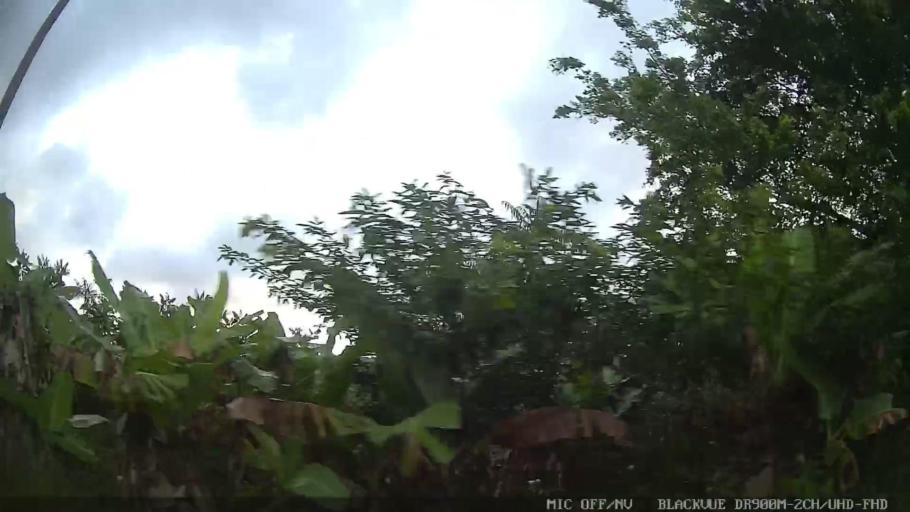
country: BR
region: Sao Paulo
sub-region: Itanhaem
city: Itanhaem
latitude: -24.0886
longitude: -46.7973
